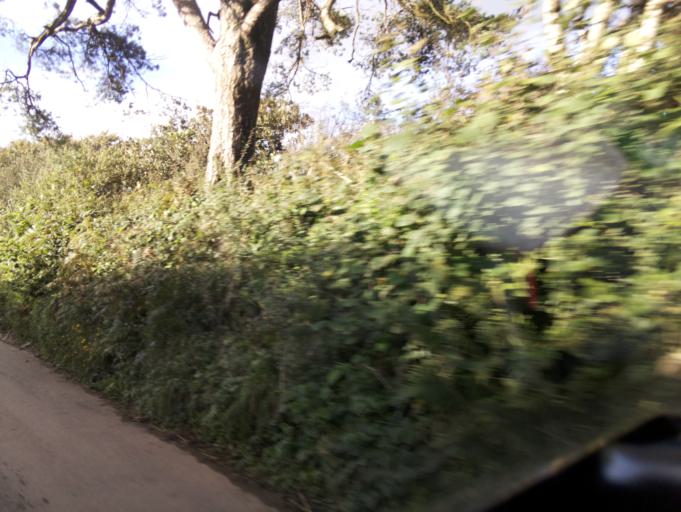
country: GB
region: England
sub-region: Devon
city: Totnes
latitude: 50.3673
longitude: -3.7416
